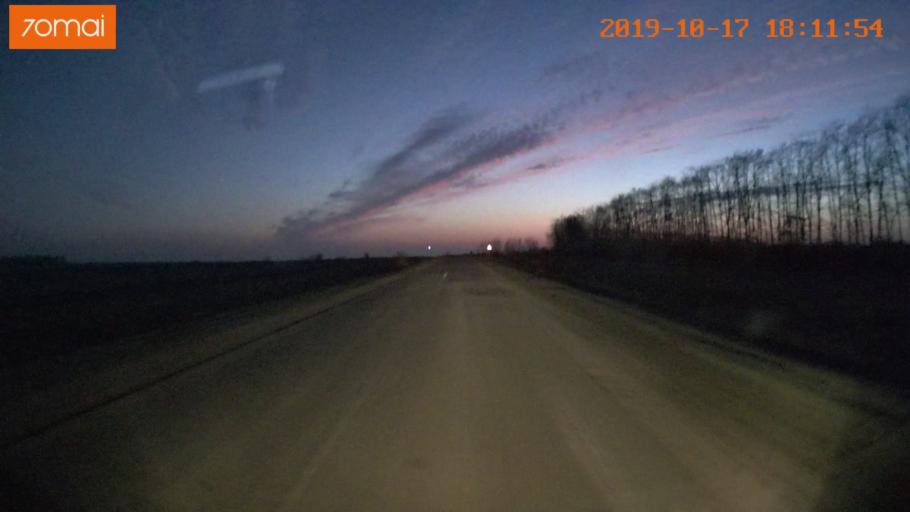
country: RU
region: Tula
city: Kurkino
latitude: 53.4131
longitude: 38.6205
